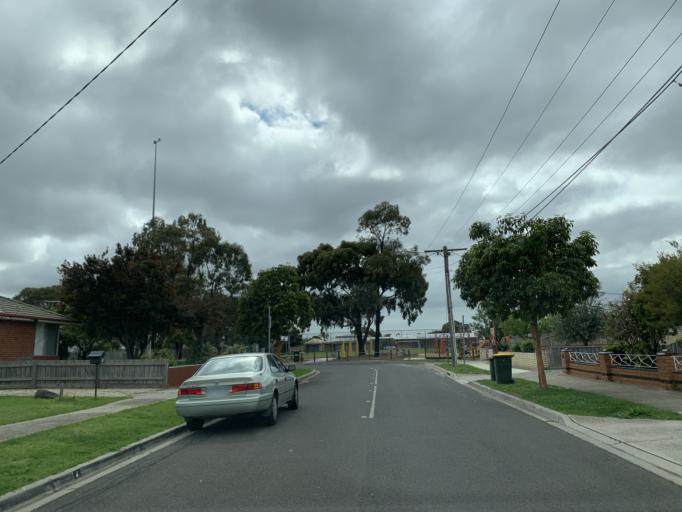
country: AU
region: Victoria
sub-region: Moonee Valley
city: Essendon West
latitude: -37.7625
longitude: 144.8572
